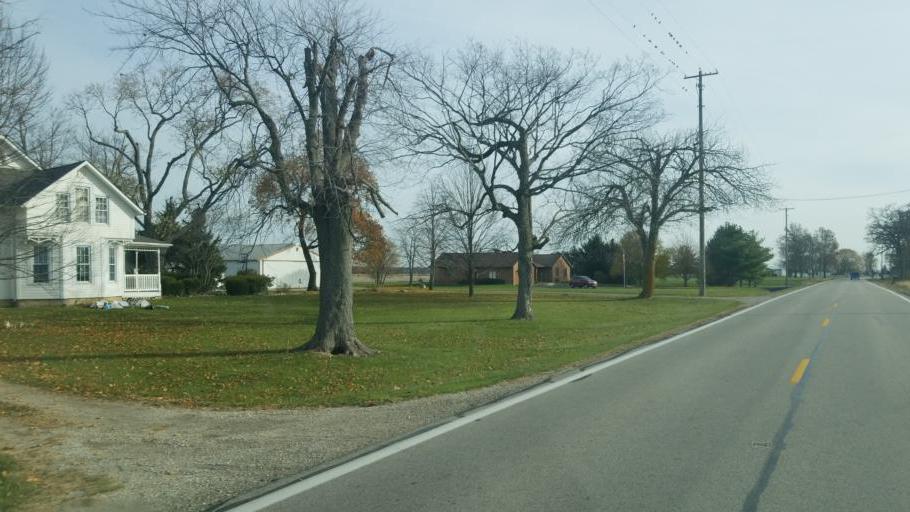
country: US
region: Ohio
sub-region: Madison County
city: Plain City
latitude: 40.1151
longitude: -83.3259
